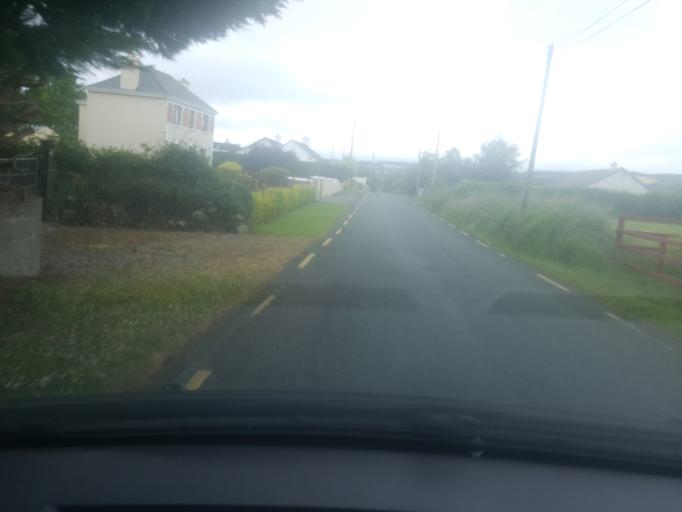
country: IE
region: Munster
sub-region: Ciarrai
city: Cill Airne
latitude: 52.0979
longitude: -9.5062
